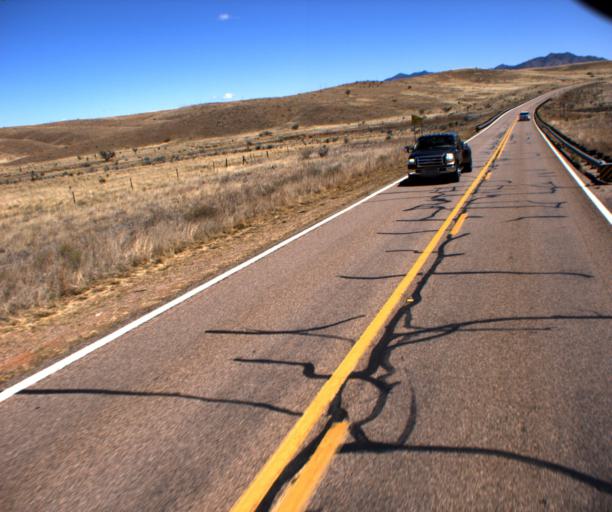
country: US
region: Arizona
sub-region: Cochise County
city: Huachuca City
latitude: 31.7081
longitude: -110.5782
